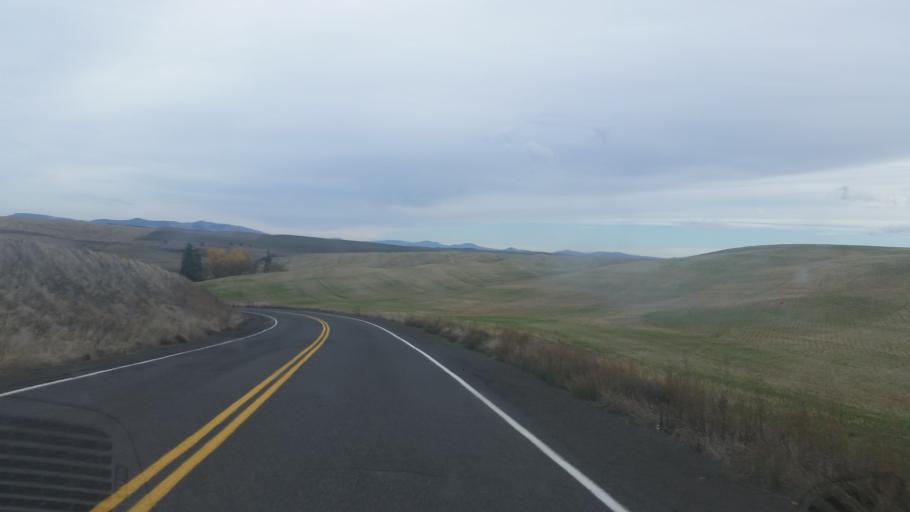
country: US
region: Washington
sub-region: Spokane County
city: Cheney
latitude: 47.2210
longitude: -117.3771
